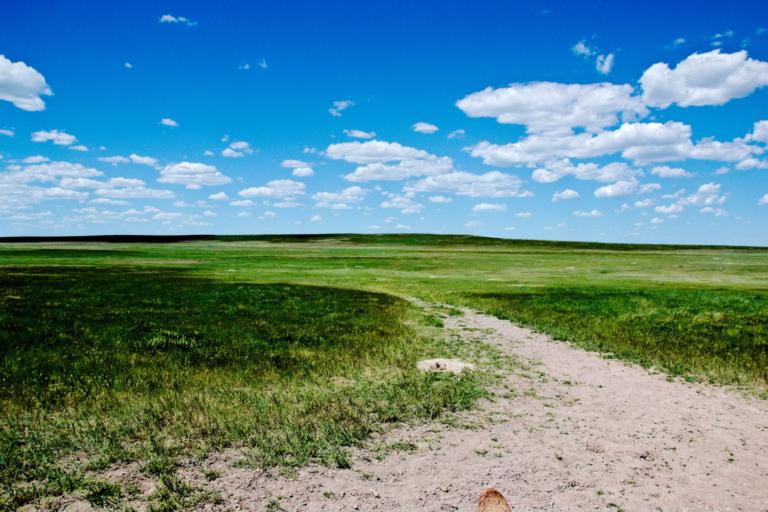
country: US
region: South Dakota
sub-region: Haakon County
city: Philip
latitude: 43.9053
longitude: -102.3071
